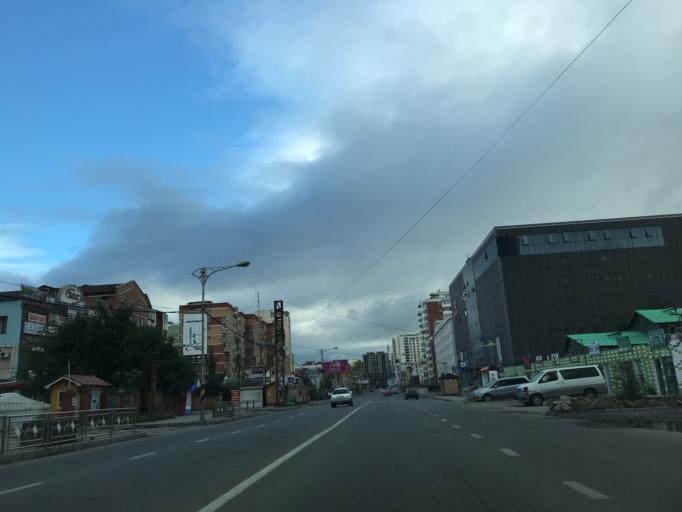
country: MN
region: Ulaanbaatar
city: Ulaanbaatar
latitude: 47.9097
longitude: 106.9435
